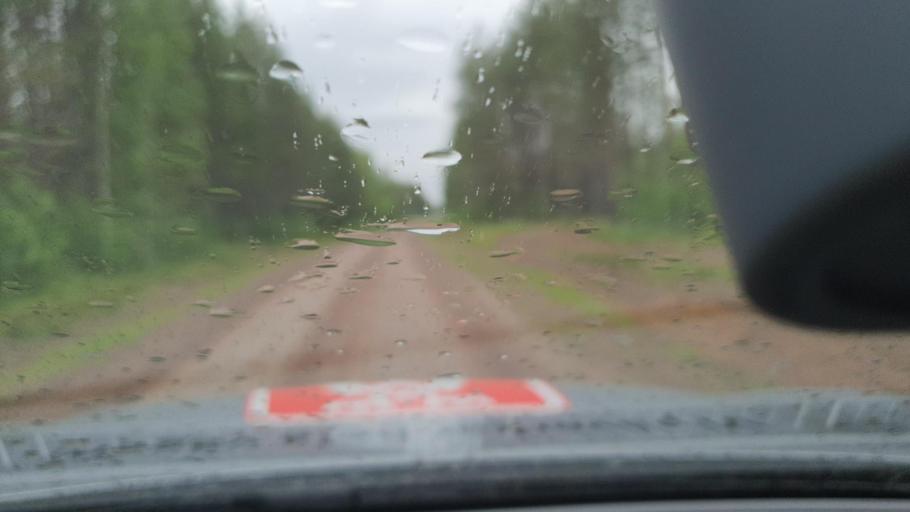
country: SE
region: Norrbotten
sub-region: Overkalix Kommun
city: OEverkalix
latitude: 66.5558
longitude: 22.7458
